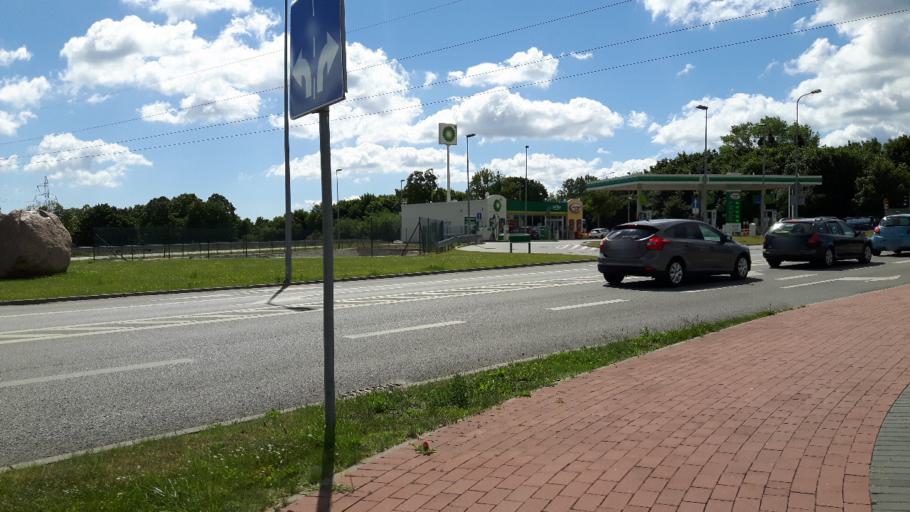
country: PL
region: Pomeranian Voivodeship
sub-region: Gdynia
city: Pogorze
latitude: 54.5646
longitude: 18.5060
